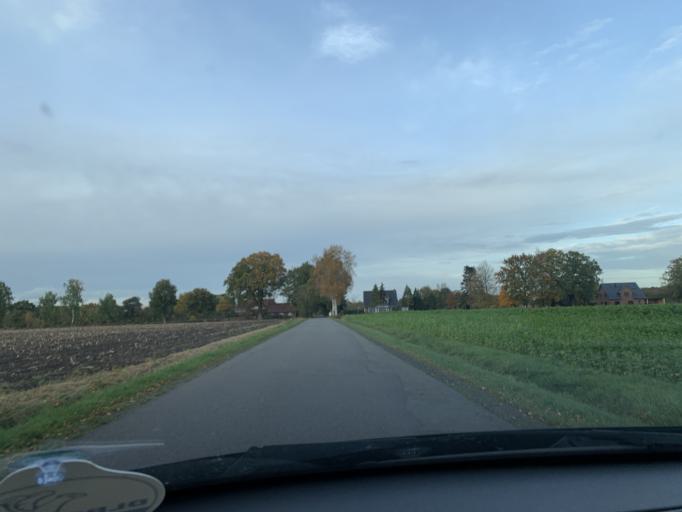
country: DE
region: Lower Saxony
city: Bad Zwischenahn
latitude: 53.2271
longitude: 8.0451
